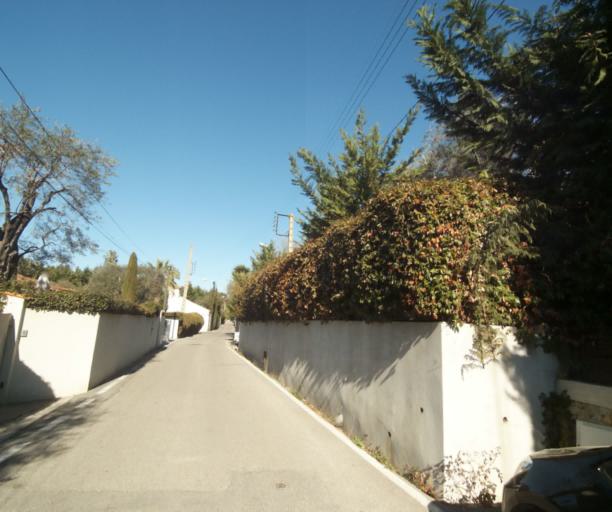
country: FR
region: Provence-Alpes-Cote d'Azur
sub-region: Departement des Alpes-Maritimes
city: Antibes
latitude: 43.5570
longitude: 7.1247
